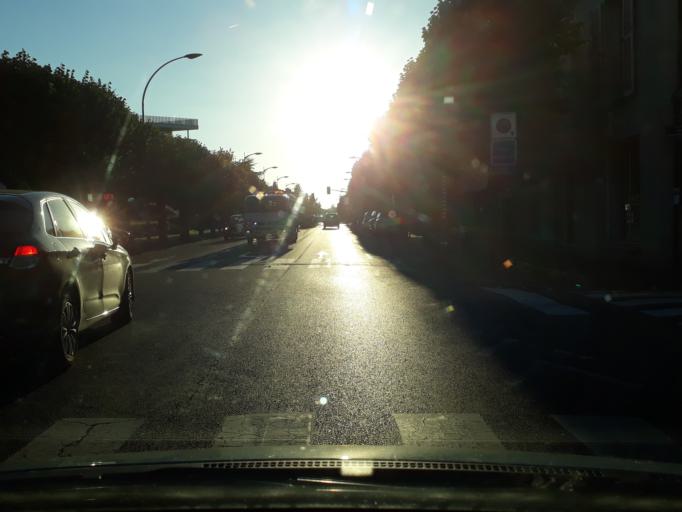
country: FR
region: Ile-de-France
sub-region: Departement de Seine-et-Marne
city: Avon
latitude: 48.4155
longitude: 2.7203
